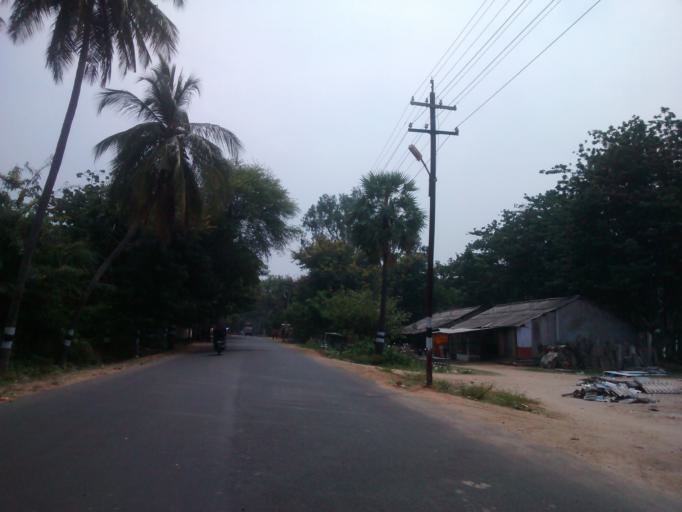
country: IN
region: Tamil Nadu
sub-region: Krishnagiri
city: Krishnagiri
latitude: 12.4744
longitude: 78.1924
